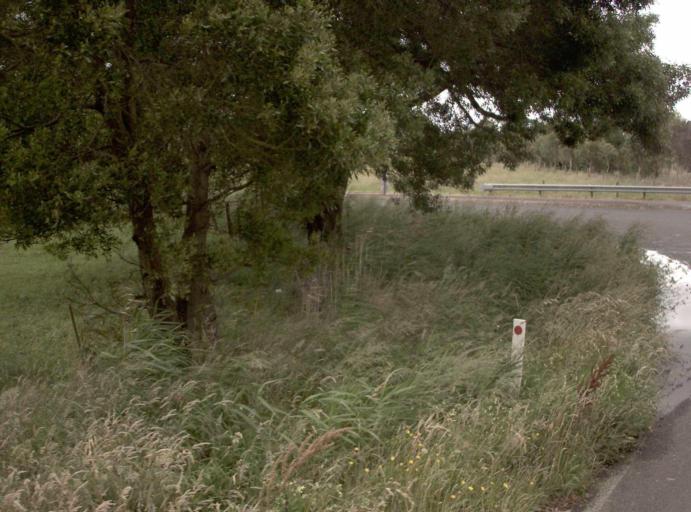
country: AU
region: Victoria
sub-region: Baw Baw
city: Warragul
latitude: -38.1617
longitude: 145.9784
